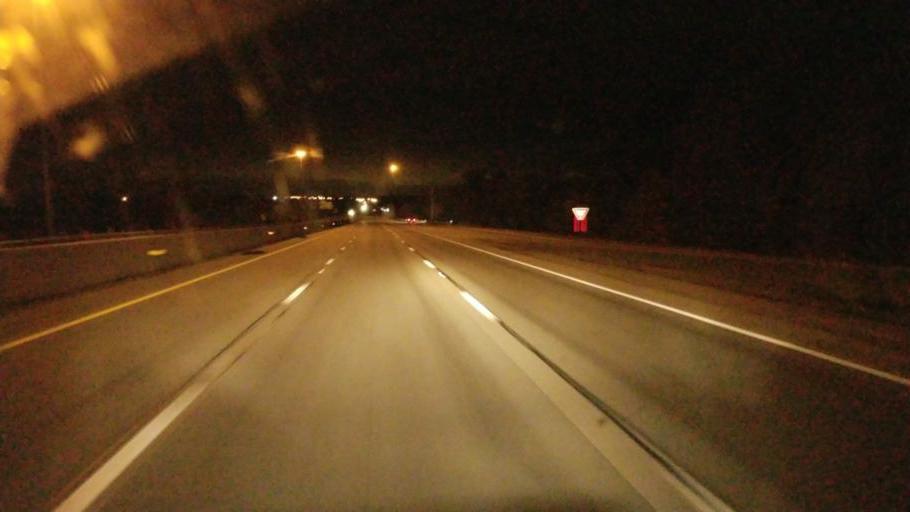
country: US
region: Ohio
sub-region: Licking County
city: Harbor Hills
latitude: 39.9441
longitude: -82.4107
